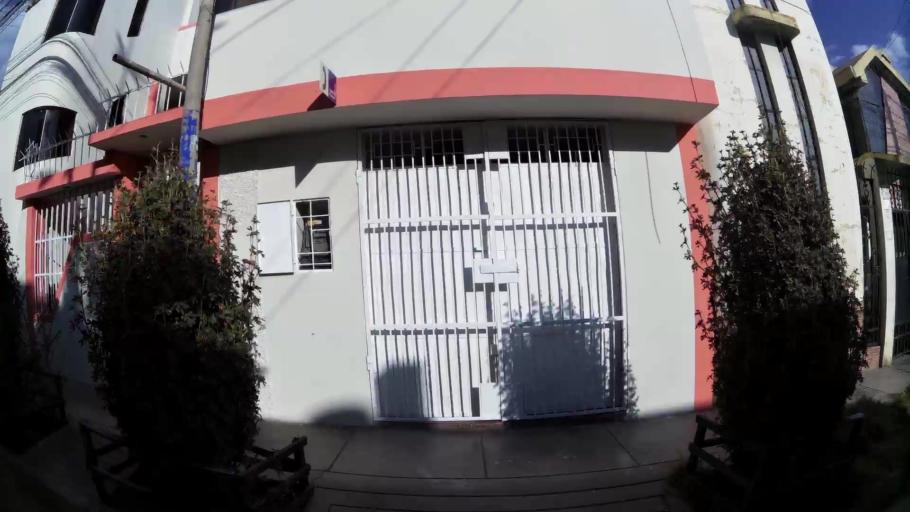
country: PE
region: Junin
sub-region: Provincia de Huancayo
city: El Tambo
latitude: -12.0564
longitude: -75.2267
